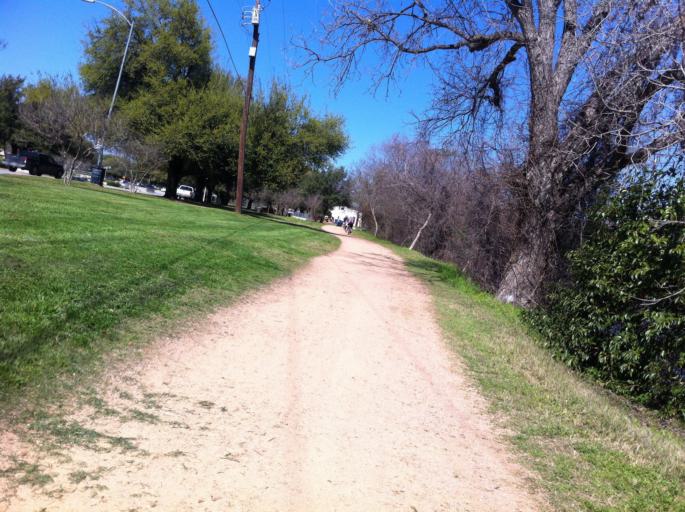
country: US
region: Texas
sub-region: Travis County
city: Austin
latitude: 30.2441
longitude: -97.7206
